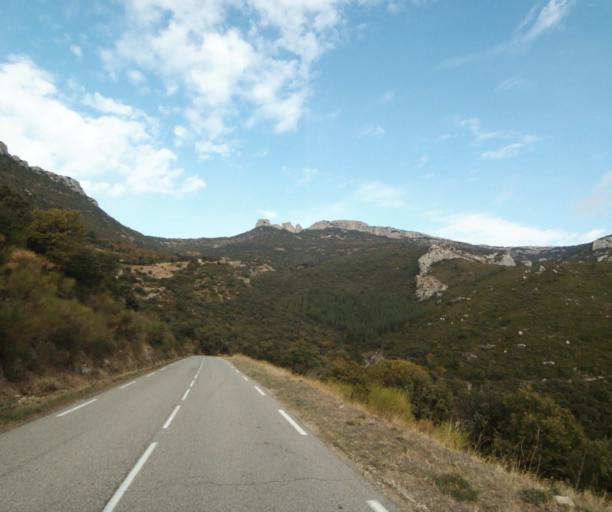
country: FR
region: Provence-Alpes-Cote d'Azur
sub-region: Departement des Bouches-du-Rhone
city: Gemenos
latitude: 43.3044
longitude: 5.6674
